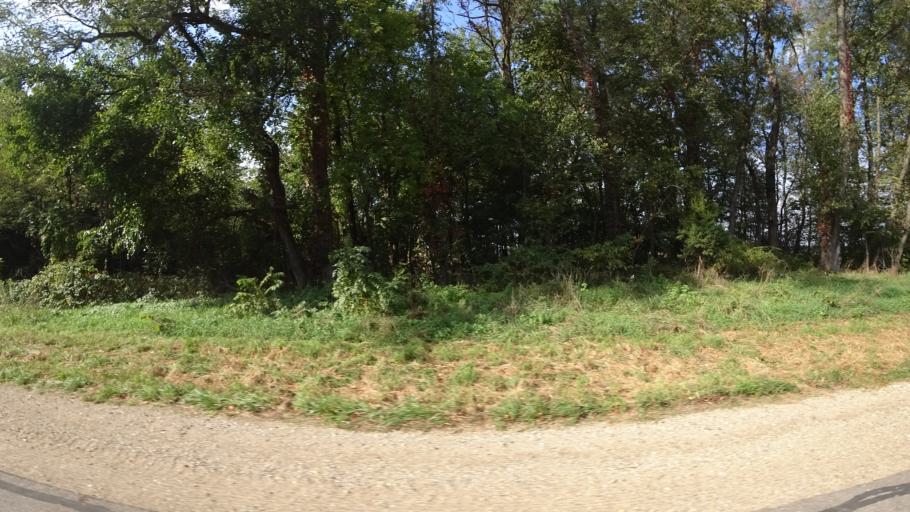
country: US
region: Michigan
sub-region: Saint Joseph County
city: Three Rivers
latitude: 41.9616
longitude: -85.5769
